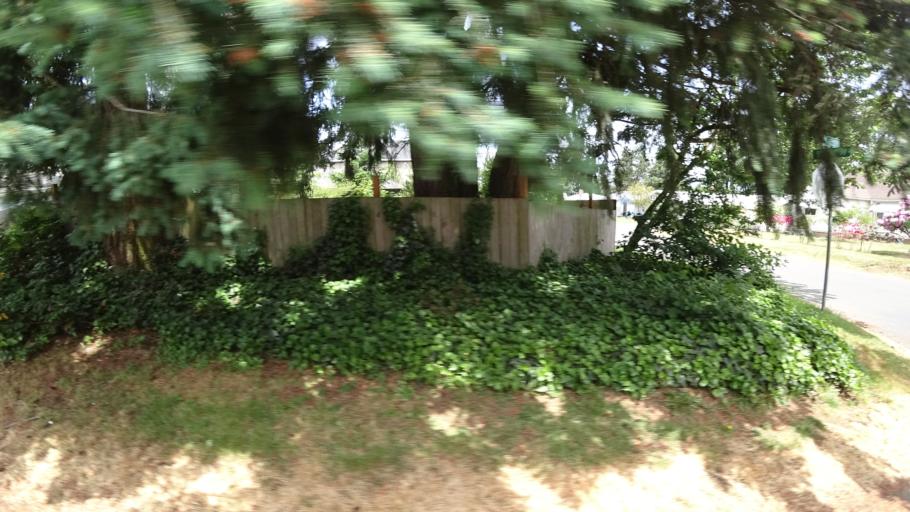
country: US
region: Oregon
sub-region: Multnomah County
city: Lents
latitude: 45.4711
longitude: -122.5973
